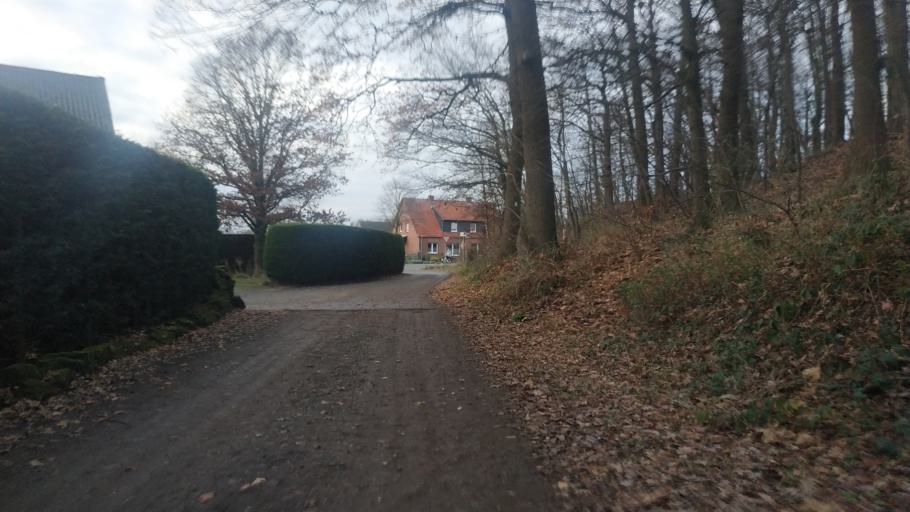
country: DE
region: North Rhine-Westphalia
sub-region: Regierungsbezirk Munster
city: Horstel
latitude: 52.2822
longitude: 7.5888
